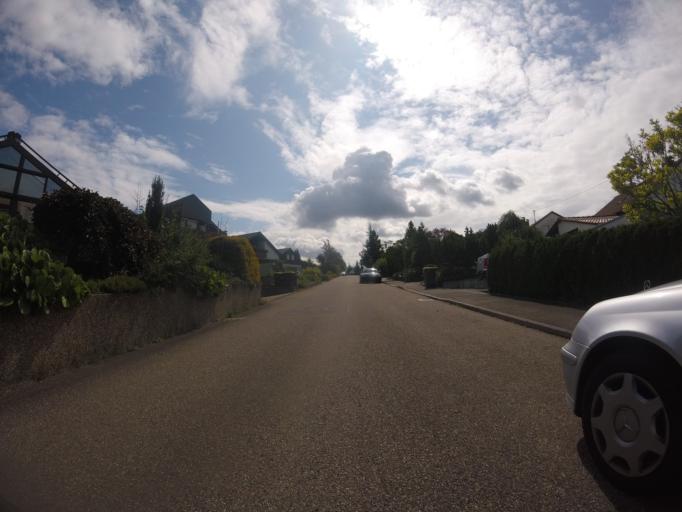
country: DE
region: Baden-Wuerttemberg
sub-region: Regierungsbezirk Stuttgart
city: Winnenden
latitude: 48.8559
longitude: 9.4084
